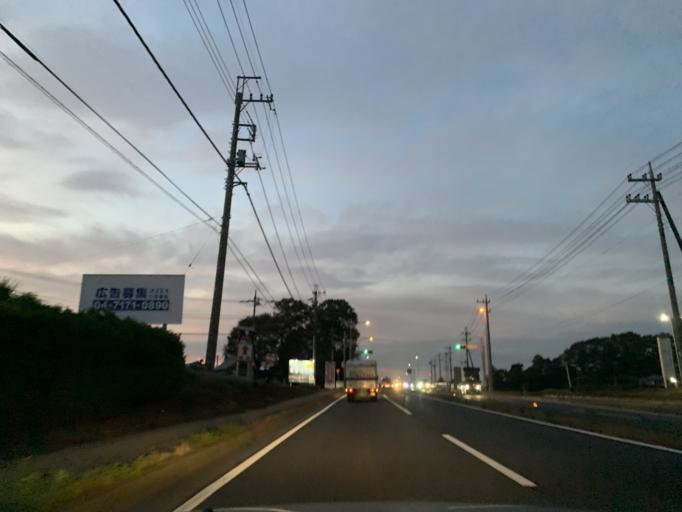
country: JP
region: Chiba
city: Nagareyama
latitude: 35.9148
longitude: 139.9290
